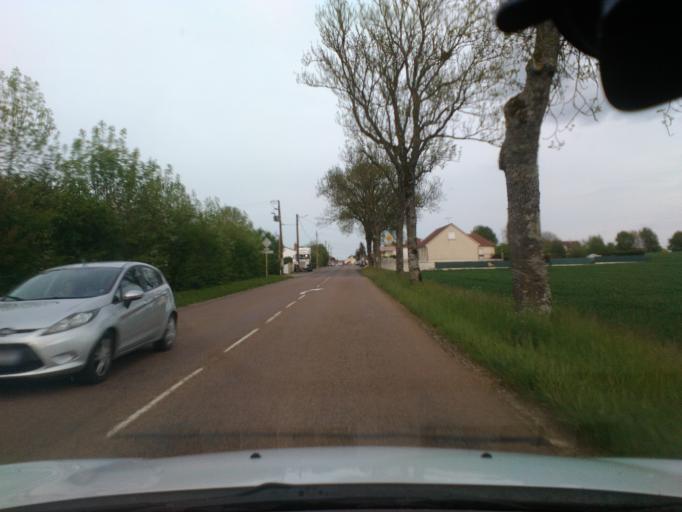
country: FR
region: Champagne-Ardenne
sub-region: Departement de la Haute-Marne
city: Chaumont
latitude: 48.1364
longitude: 5.0797
